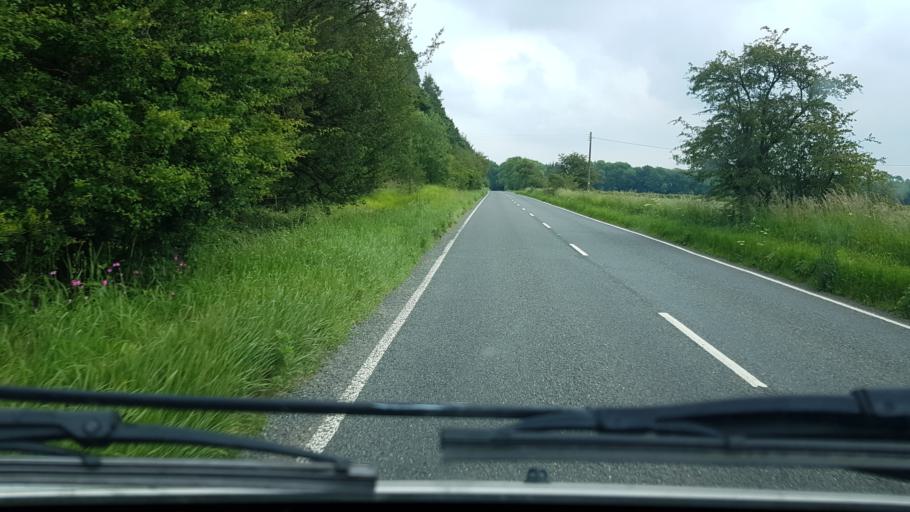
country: GB
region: England
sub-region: Gloucestershire
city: Donnington
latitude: 51.9870
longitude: -1.7719
